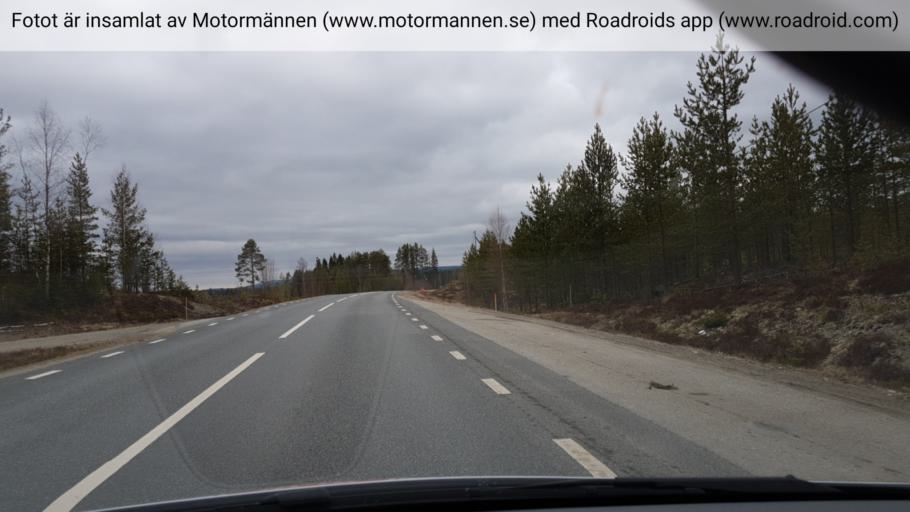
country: SE
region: Vaesternorrland
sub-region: OErnskoeldsviks Kommun
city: Bredbyn
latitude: 63.7874
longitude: 18.4946
